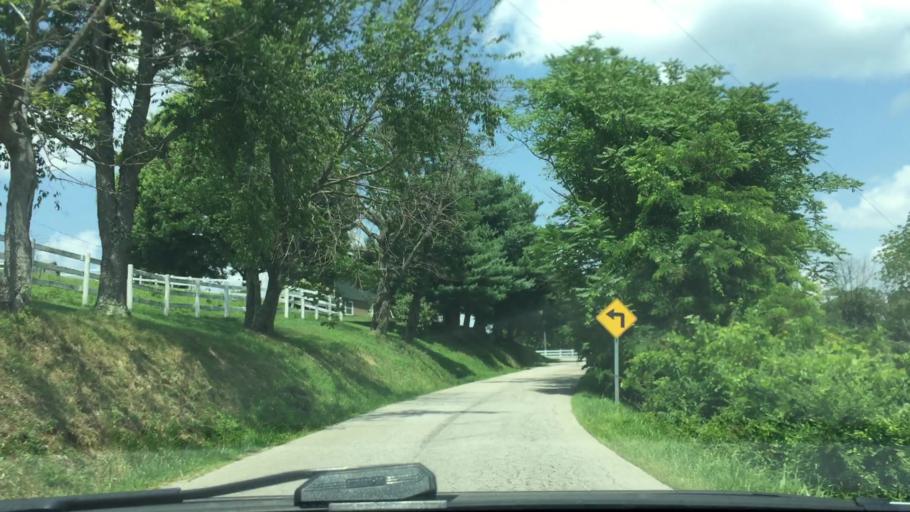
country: US
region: West Virginia
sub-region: Wetzel County
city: New Martinsville
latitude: 39.7158
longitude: -80.7484
